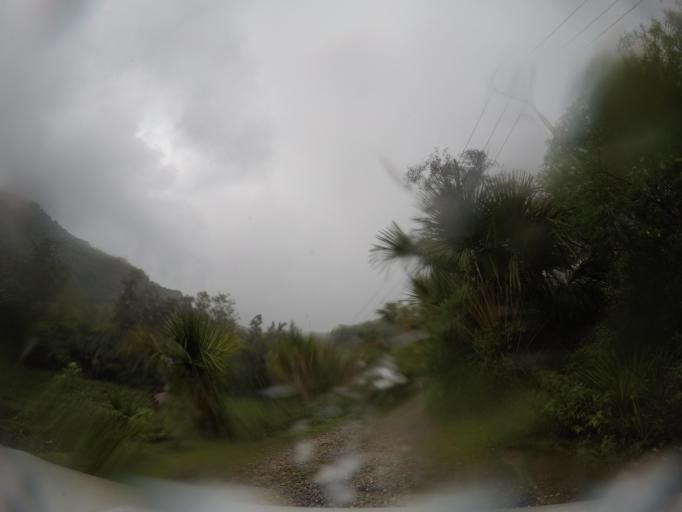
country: TL
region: Baucau
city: Venilale
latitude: -8.6423
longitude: 126.4346
